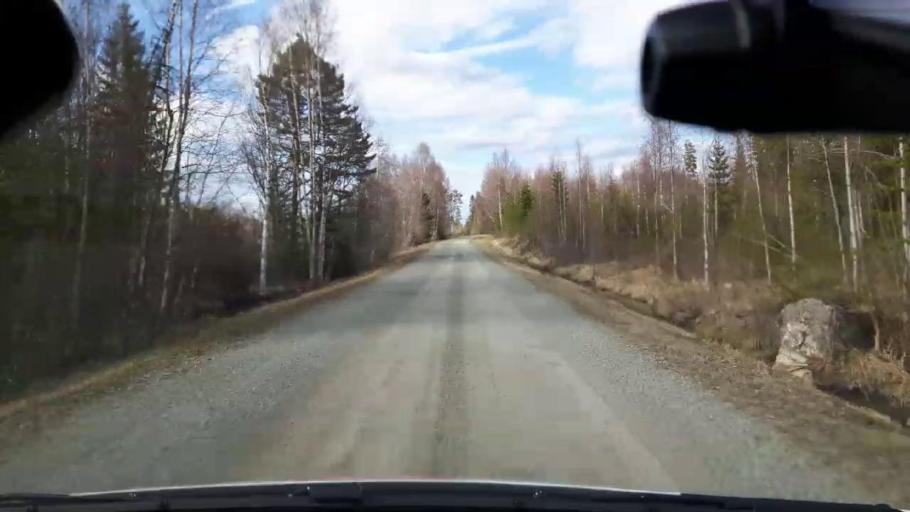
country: SE
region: Jaemtland
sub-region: Bergs Kommun
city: Hoverberg
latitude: 62.7505
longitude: 14.6631
